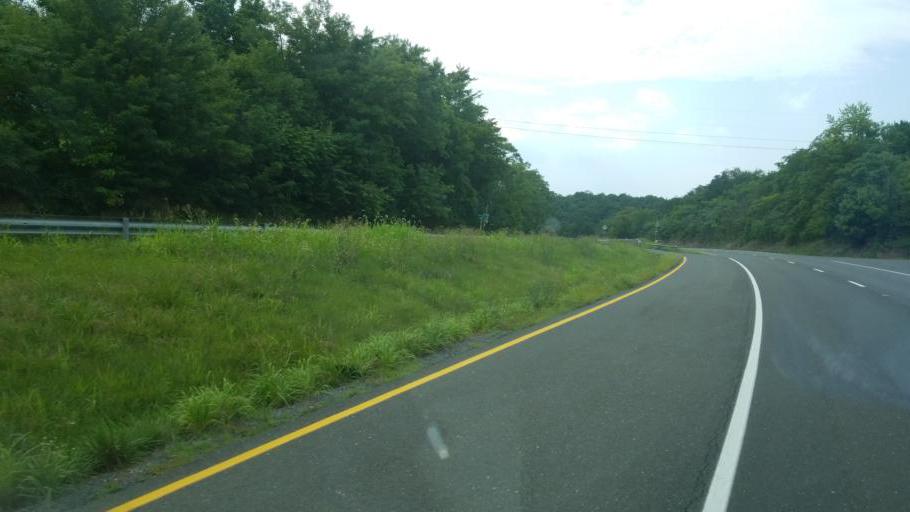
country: US
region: Virginia
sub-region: City of Winchester
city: Winchester
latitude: 39.2605
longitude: -78.2225
